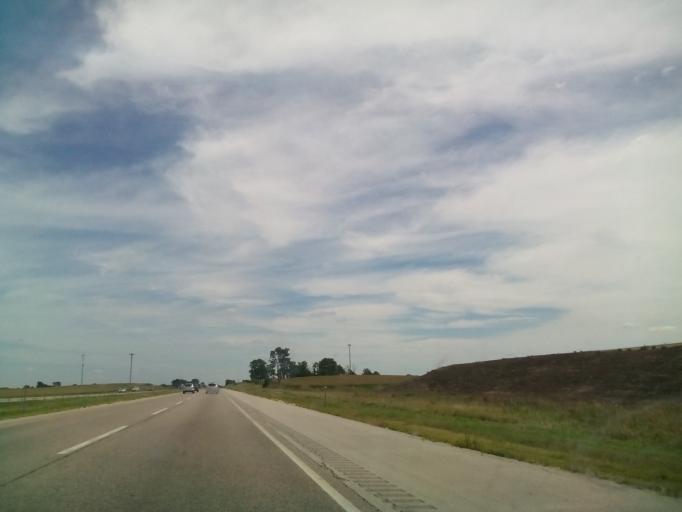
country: US
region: Illinois
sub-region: DeKalb County
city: Cortland
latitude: 41.9008
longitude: -88.6696
